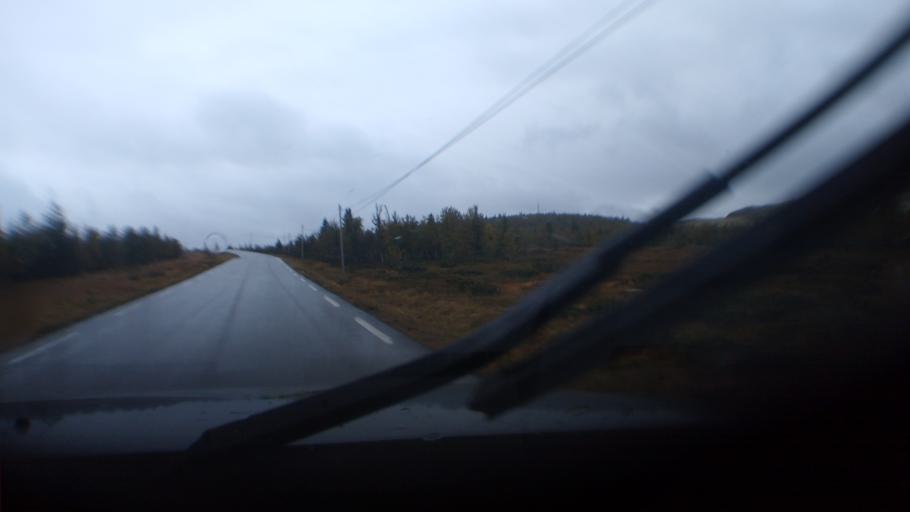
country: NO
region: Oppland
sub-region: Ringebu
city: Ringebu
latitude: 61.6327
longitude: 10.0926
